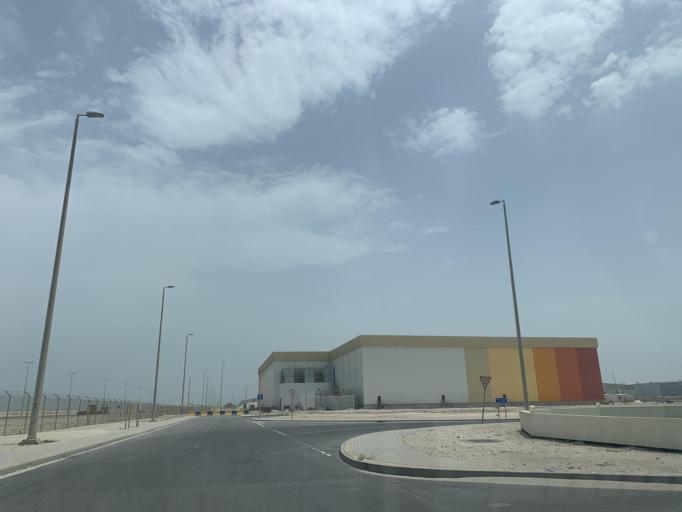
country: BH
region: Muharraq
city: Al Hadd
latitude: 26.2248
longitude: 50.6827
